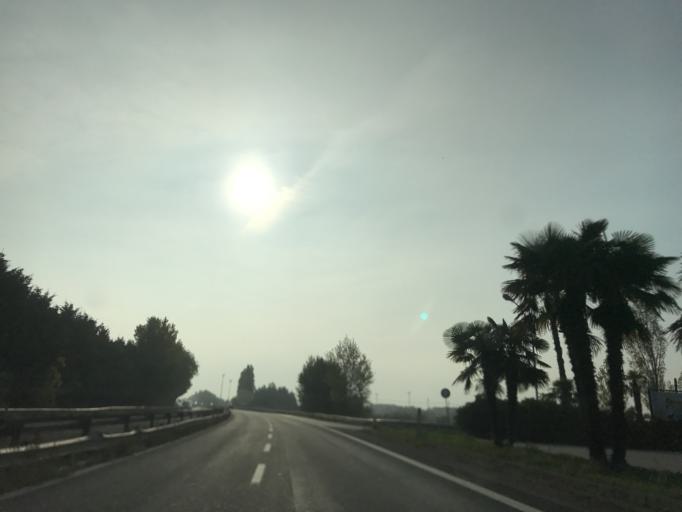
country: IT
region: Emilia-Romagna
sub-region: Forli-Cesena
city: San Mauro a Mare
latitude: 44.1500
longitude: 12.4441
